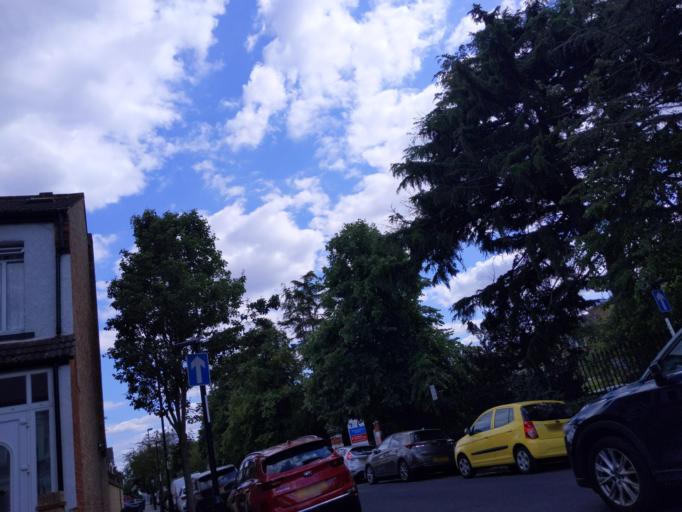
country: GB
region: England
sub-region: Greater London
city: Croydon
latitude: 51.3905
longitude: -0.1090
